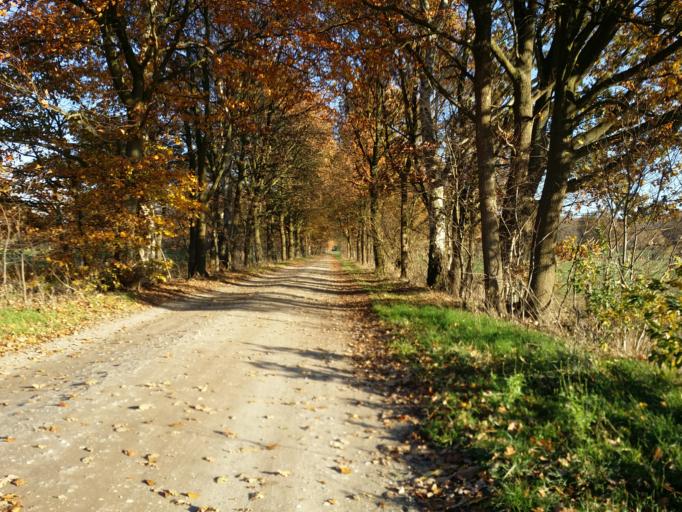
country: DE
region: Lower Saxony
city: Hellwege
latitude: 53.0353
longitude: 9.2077
